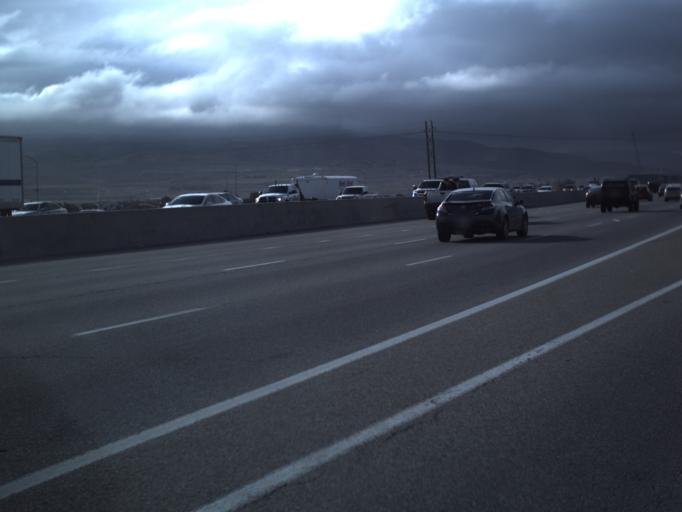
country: US
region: Utah
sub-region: Utah County
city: Lehi
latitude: 40.4119
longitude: -111.8654
